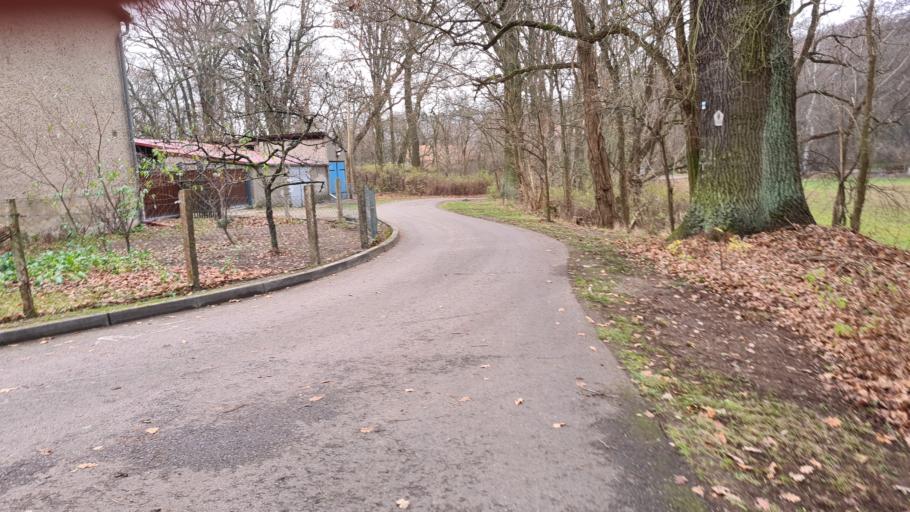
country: DE
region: Brandenburg
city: Schenkendobern
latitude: 51.9733
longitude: 14.6513
